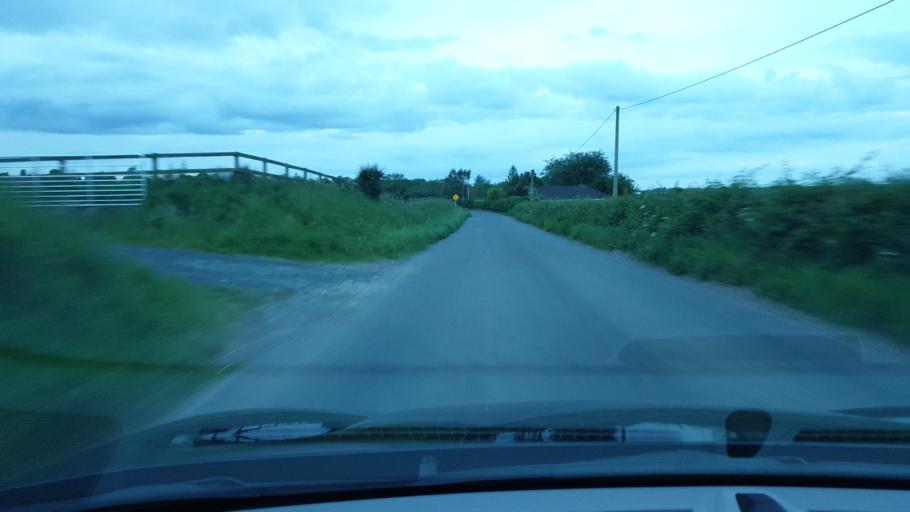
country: IE
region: Leinster
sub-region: An Mhi
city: Ashbourne
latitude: 53.5699
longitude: -6.3988
